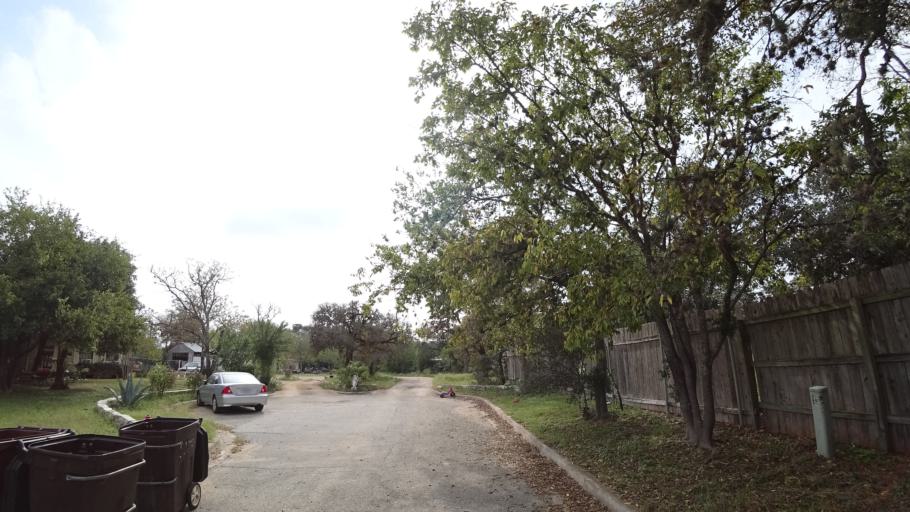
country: US
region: Texas
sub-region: Williamson County
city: Round Rock
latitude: 30.4956
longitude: -97.6938
